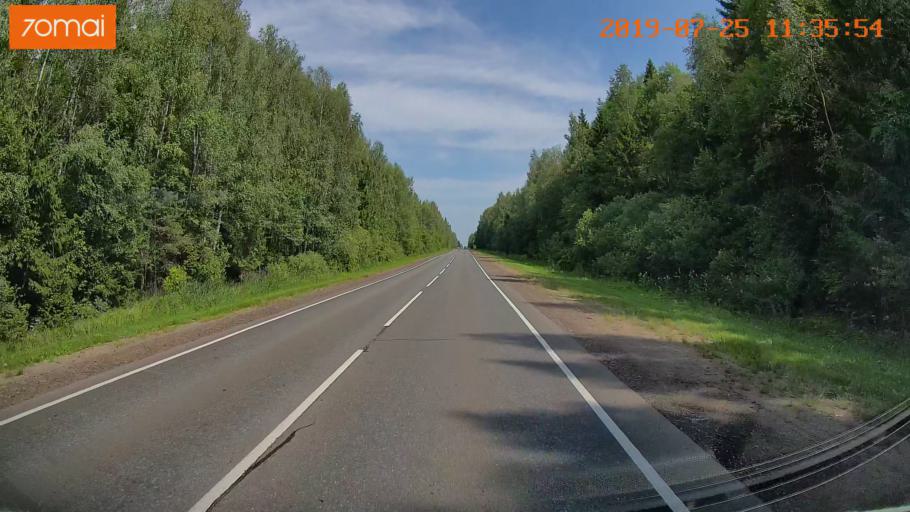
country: RU
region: Ivanovo
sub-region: Privolzhskiy Rayon
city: Ples
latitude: 57.4171
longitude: 41.4381
